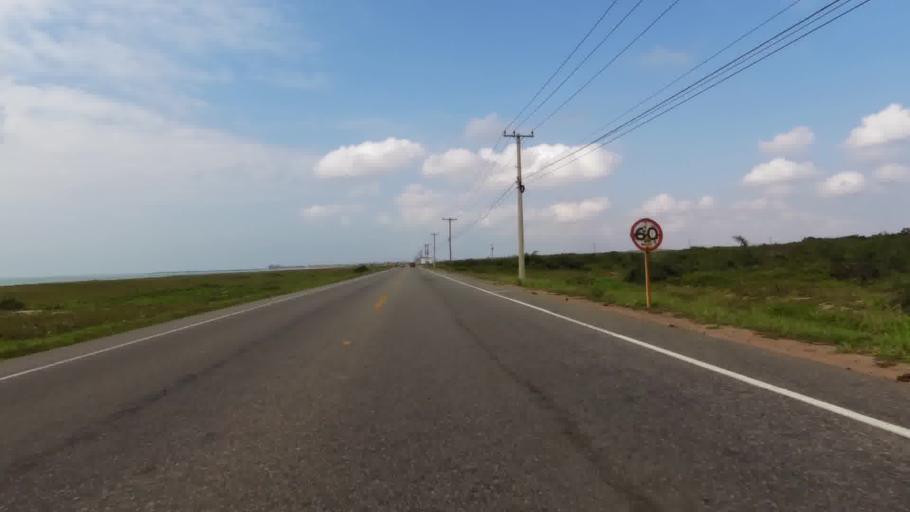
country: BR
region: Espirito Santo
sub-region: Itapemirim
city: Itapemirim
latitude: -20.9771
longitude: -40.8117
